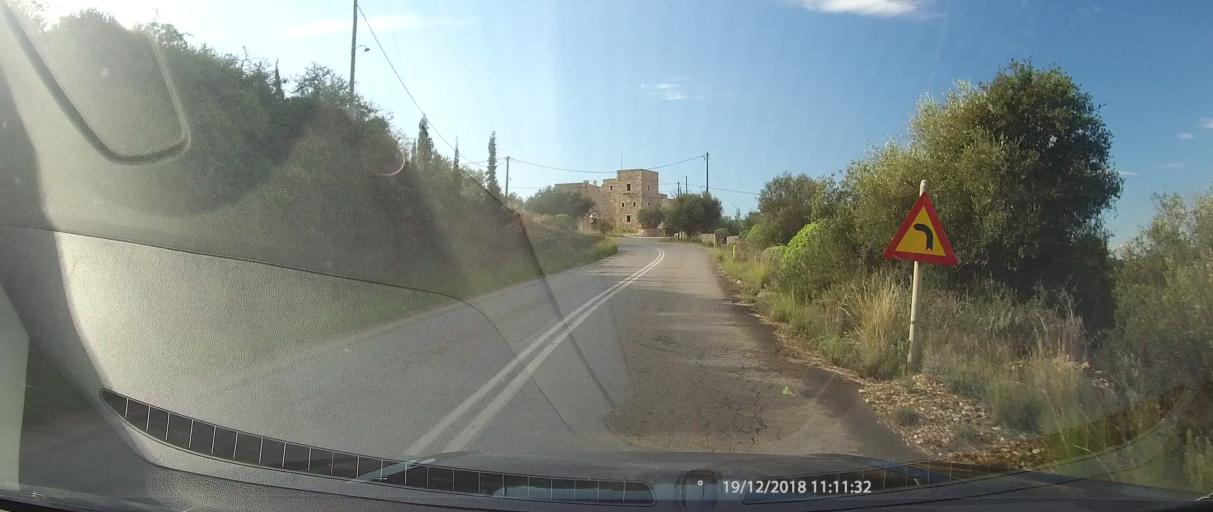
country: GR
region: Peloponnese
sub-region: Nomos Messinias
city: Kardamyli
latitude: 36.8194
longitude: 22.3020
